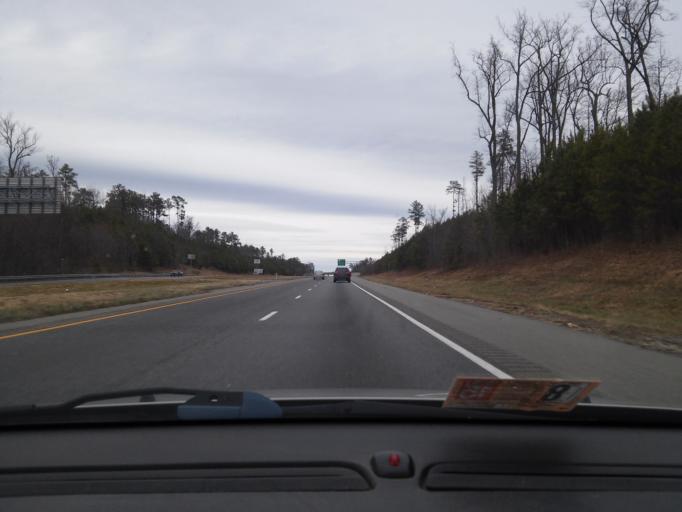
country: US
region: Virginia
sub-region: Henrico County
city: Short Pump
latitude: 37.5797
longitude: -77.6775
